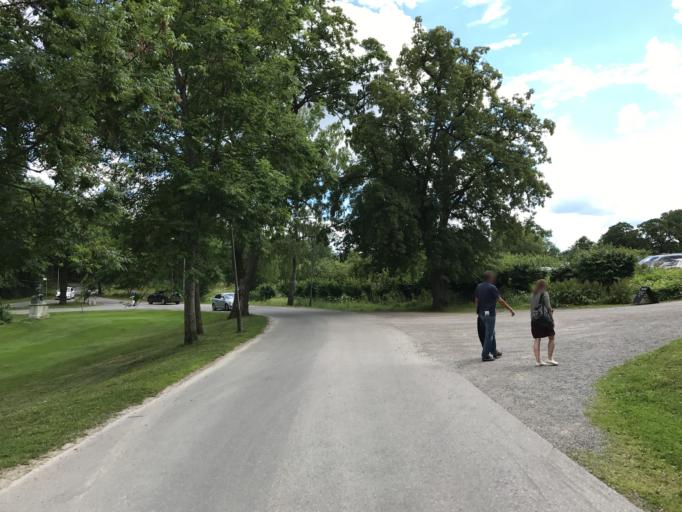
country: SE
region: Stockholm
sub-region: Stockholms Kommun
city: OEstermalm
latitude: 59.3278
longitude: 18.1166
